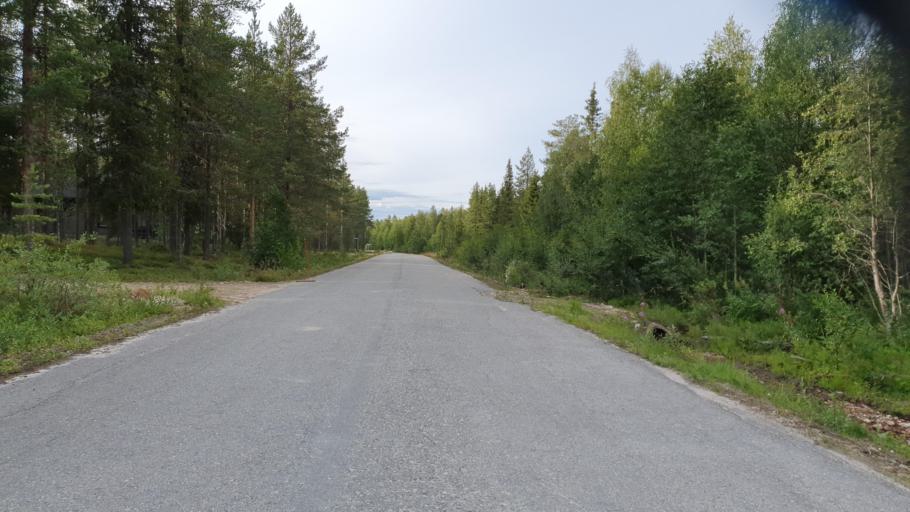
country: FI
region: Lapland
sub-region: Tunturi-Lappi
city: Kolari
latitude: 67.5958
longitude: 24.1655
